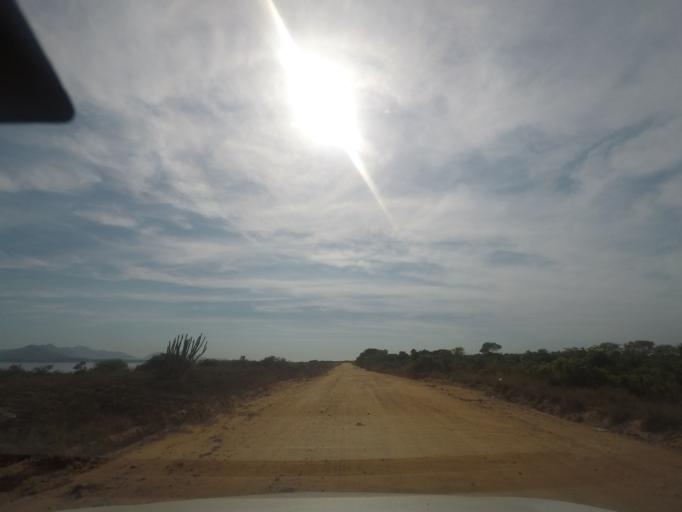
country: BR
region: Rio de Janeiro
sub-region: Marica
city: Marica
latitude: -22.9578
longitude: -42.8824
